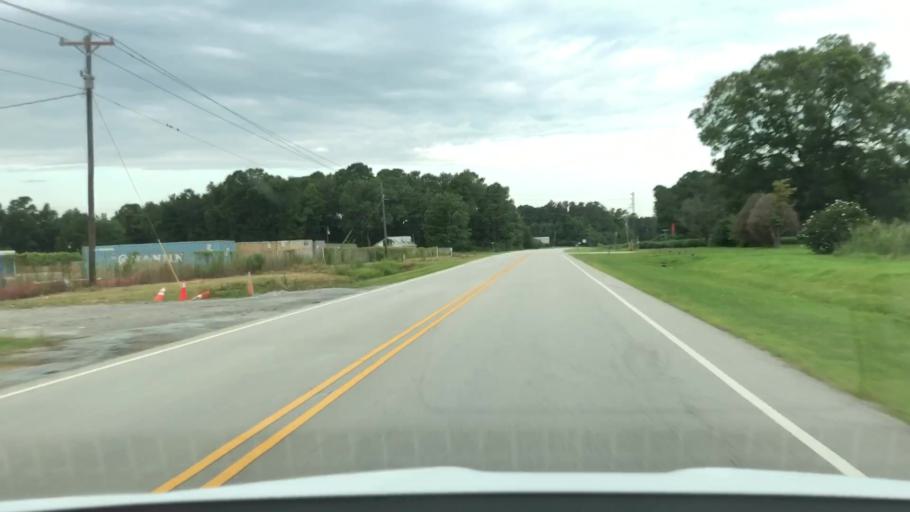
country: US
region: North Carolina
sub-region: Jones County
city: Trenton
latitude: 35.0355
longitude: -77.3375
